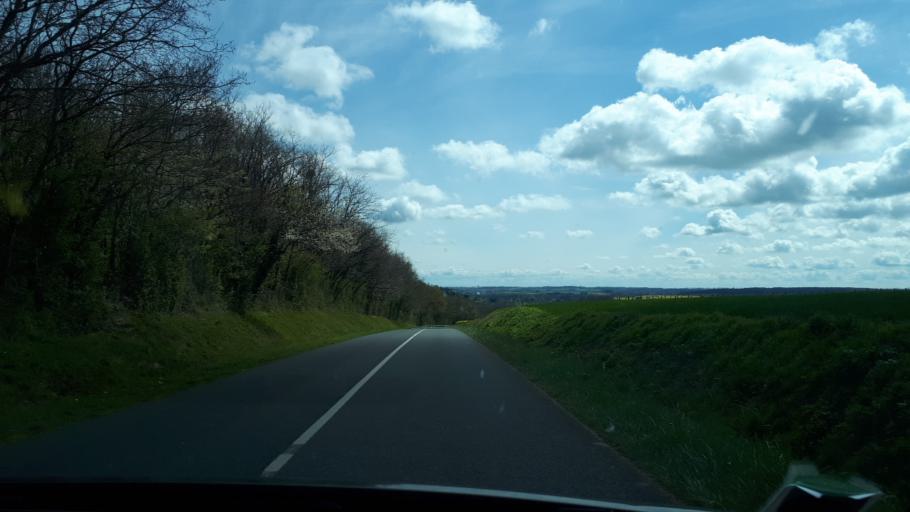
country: FR
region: Centre
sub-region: Departement du Loir-et-Cher
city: Lunay
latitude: 47.8165
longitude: 0.9449
